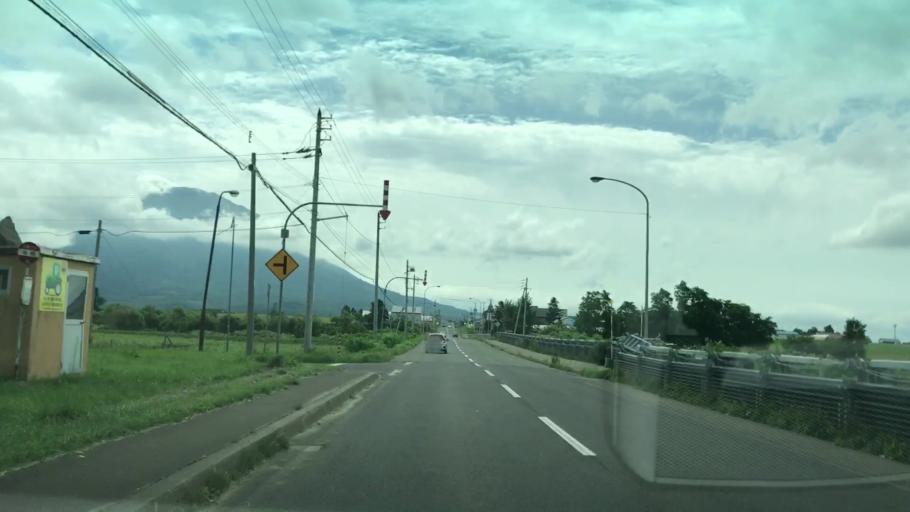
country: JP
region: Hokkaido
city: Niseko Town
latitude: 42.9283
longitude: 140.7756
